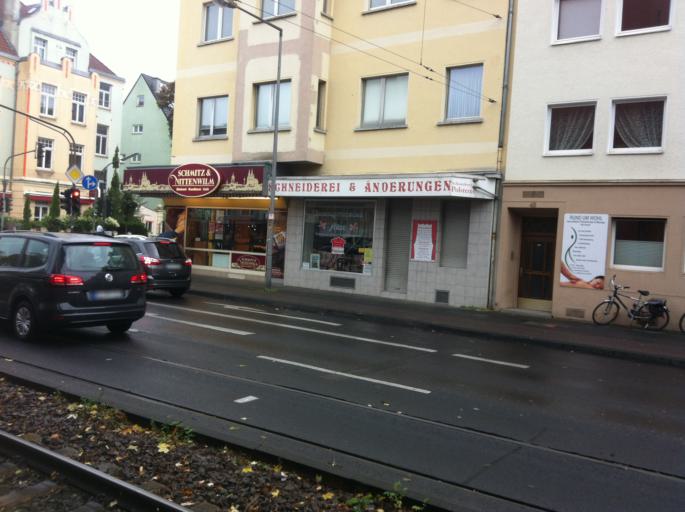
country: DE
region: North Rhine-Westphalia
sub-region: Regierungsbezirk Koln
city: Neustadt/Sued
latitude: 50.9236
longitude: 6.9124
